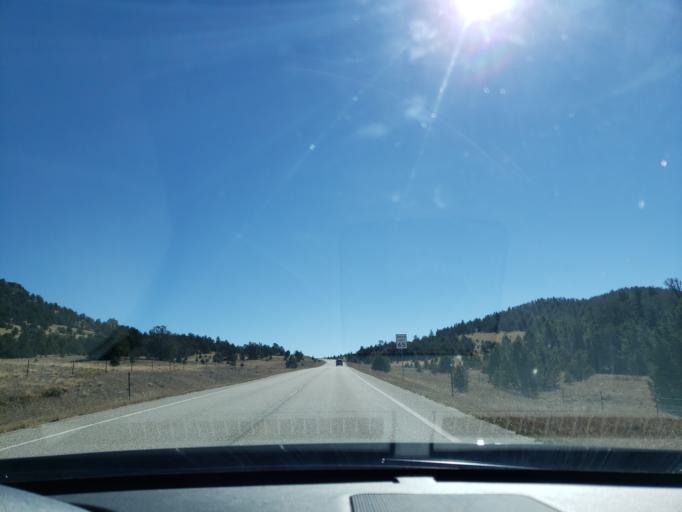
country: US
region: Colorado
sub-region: Chaffee County
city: Salida
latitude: 38.8435
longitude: -105.6418
